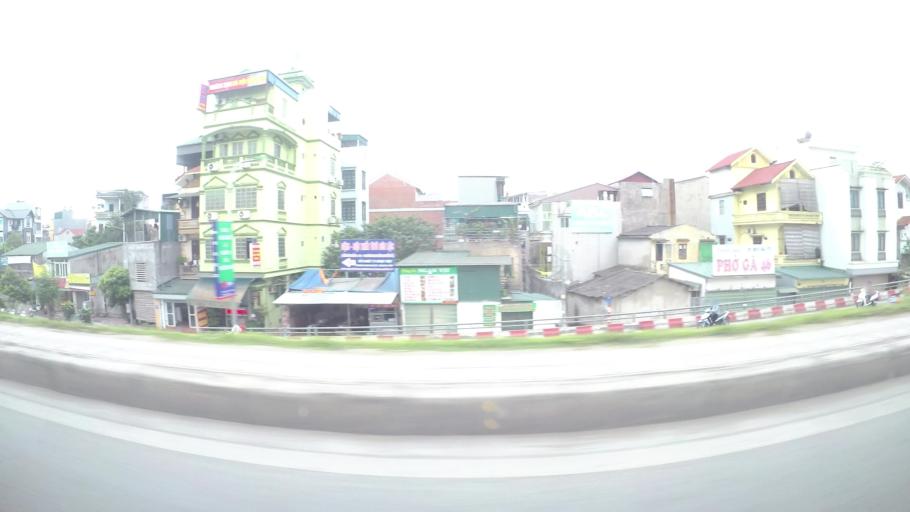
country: VN
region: Ha Noi
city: Hoan Kiem
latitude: 21.0484
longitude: 105.8653
